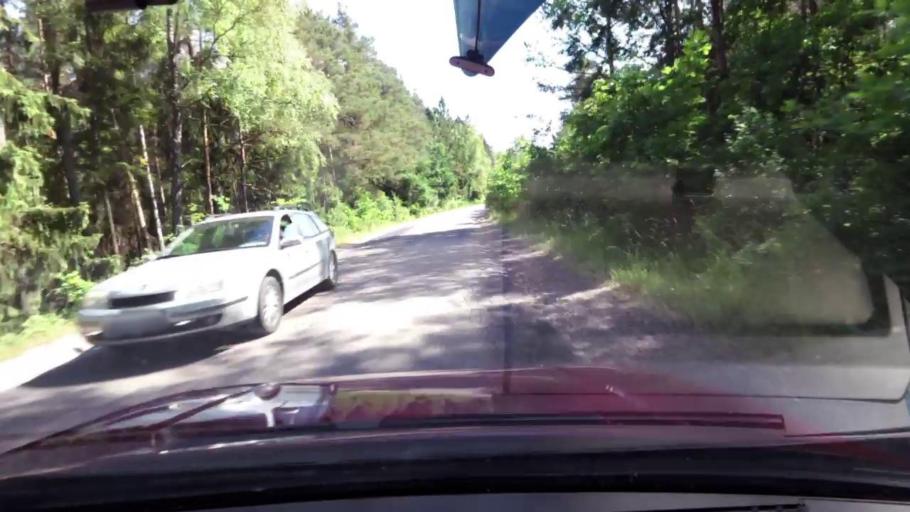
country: PL
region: Pomeranian Voivodeship
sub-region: Powiat slupski
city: Kepice
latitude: 54.3295
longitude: 16.9618
